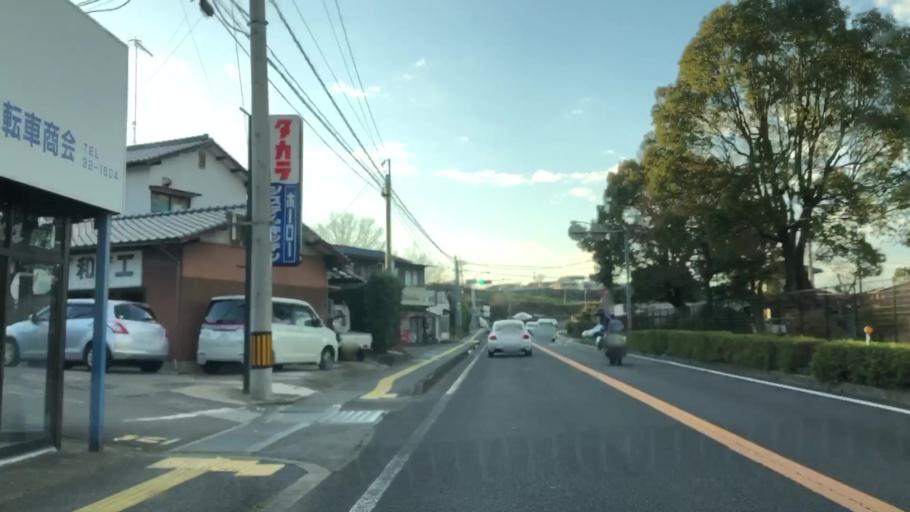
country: JP
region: Oita
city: Bungo-Takada-shi
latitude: 33.5351
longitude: 131.3155
